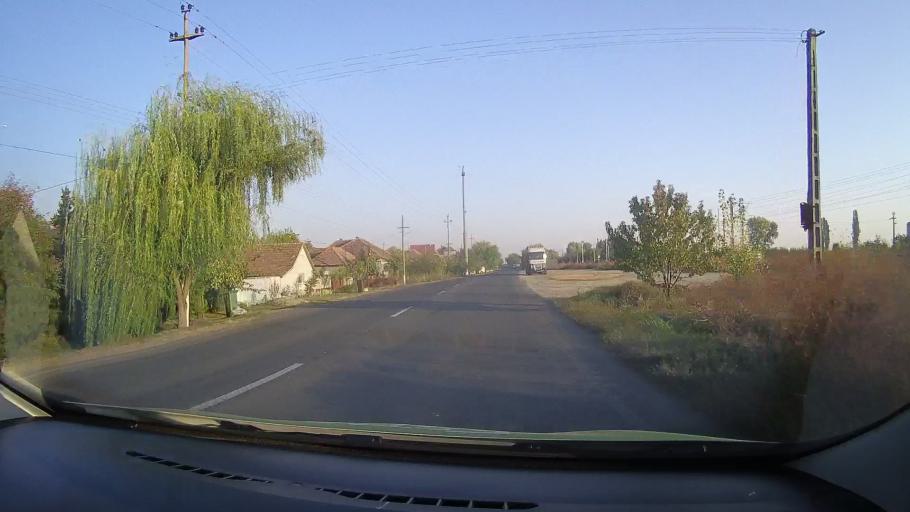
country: RO
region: Arad
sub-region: Comuna Sofronea
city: Sofronea
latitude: 46.2808
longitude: 21.3135
